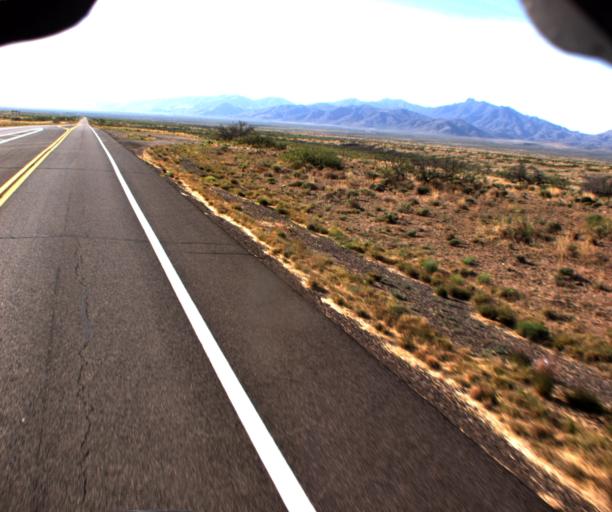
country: US
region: Arizona
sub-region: Cochise County
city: Willcox
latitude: 32.3903
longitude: -109.6624
